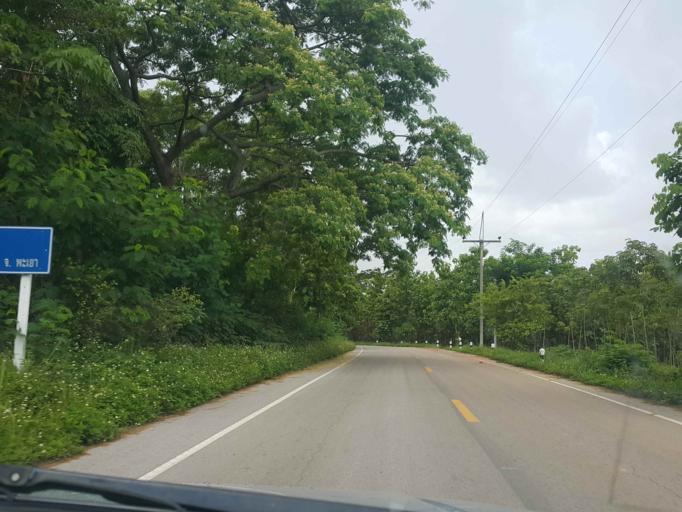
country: TH
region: Phayao
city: Dok Kham Tai
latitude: 19.0454
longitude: 99.9520
